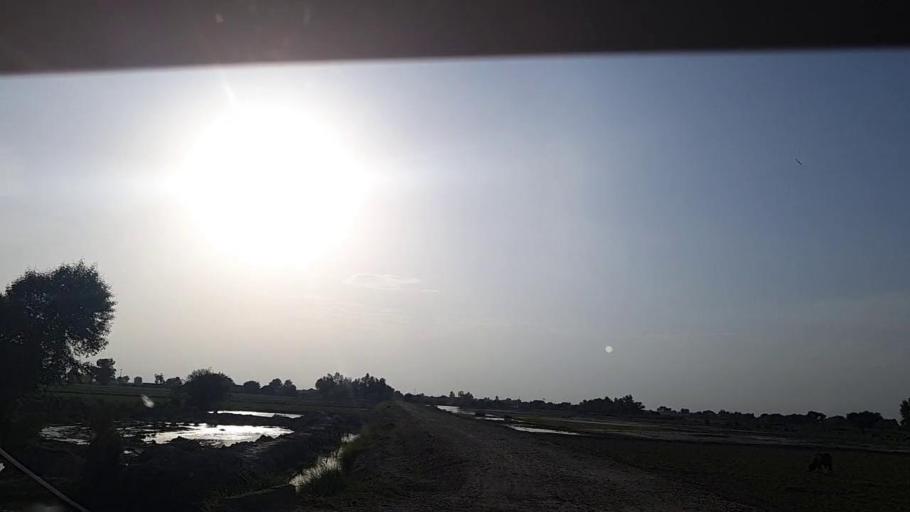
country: PK
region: Sindh
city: Khanpur
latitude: 27.8063
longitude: 69.3342
